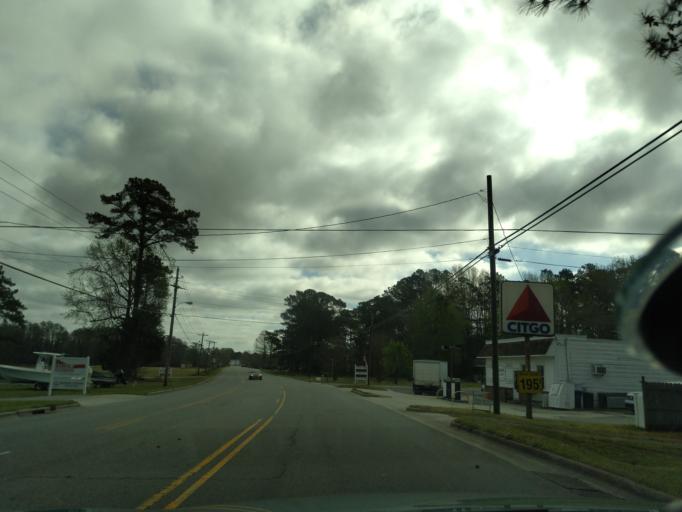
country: US
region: North Carolina
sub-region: Chowan County
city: Edenton
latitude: 36.0567
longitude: -76.6304
